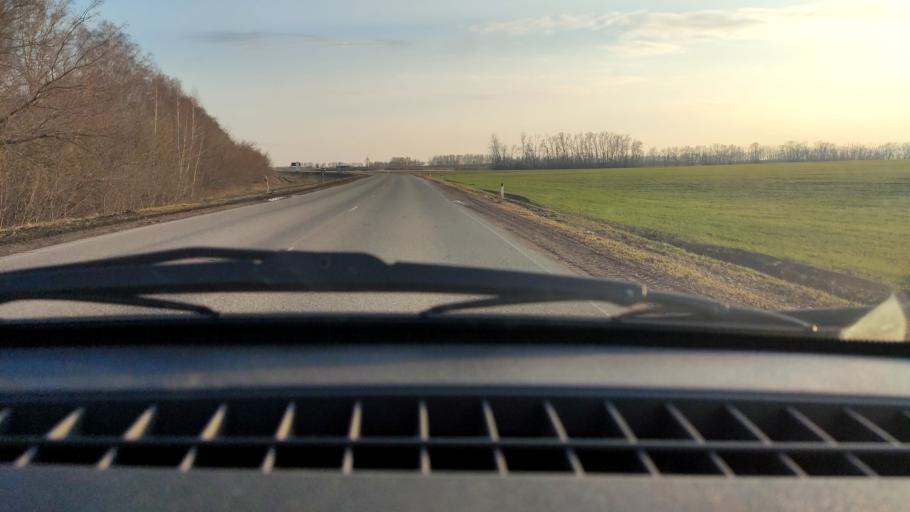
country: RU
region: Bashkortostan
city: Chishmy
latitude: 54.4958
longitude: 55.2790
